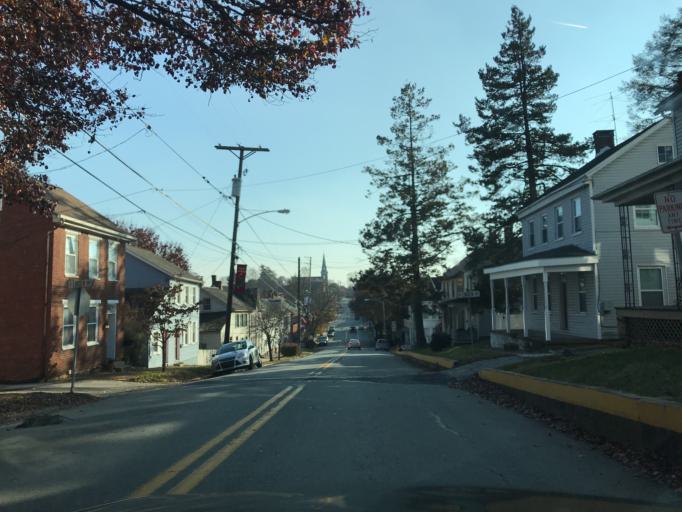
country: US
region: Pennsylvania
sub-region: York County
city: Shrewsbury
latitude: 39.7708
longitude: -76.6805
